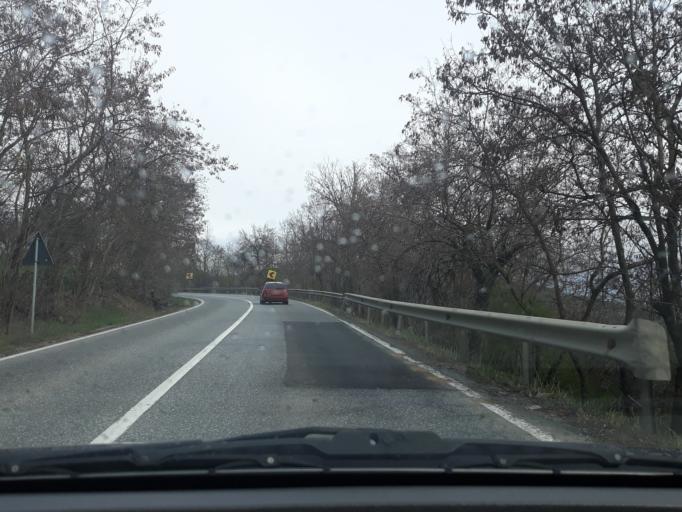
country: RO
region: Harghita
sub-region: Comuna Lupeni
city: Lupeni
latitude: 46.4079
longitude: 25.2157
